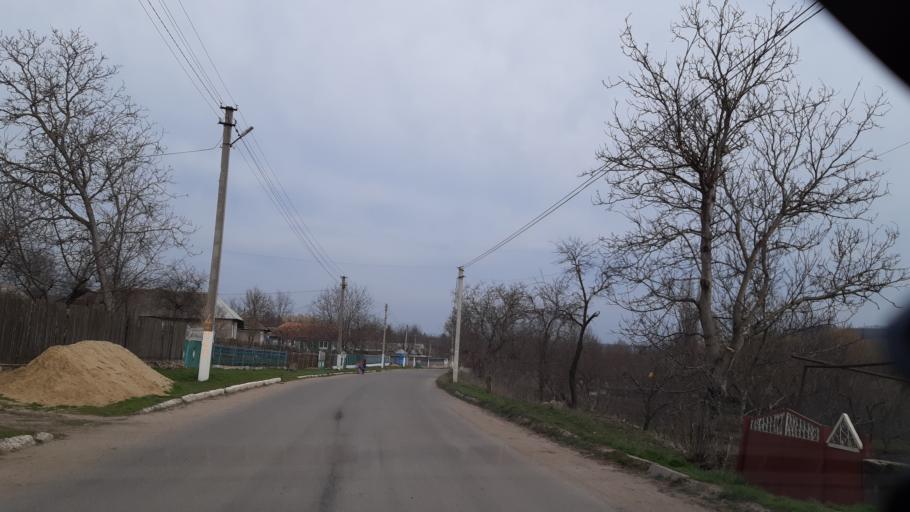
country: MD
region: Soldanesti
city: Soldanesti
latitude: 47.6853
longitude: 28.7553
